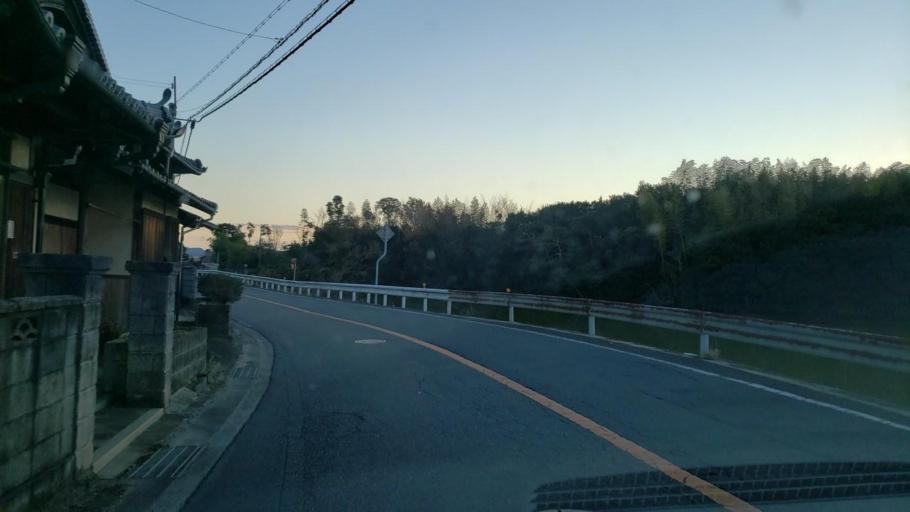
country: JP
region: Hyogo
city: Fukura
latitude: 34.3265
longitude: 134.7724
